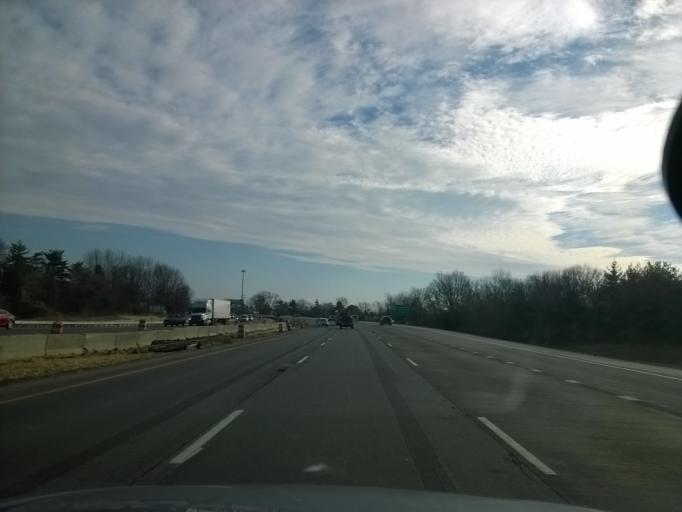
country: US
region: Indiana
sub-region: Marion County
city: Southport
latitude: 39.6746
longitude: -86.0996
